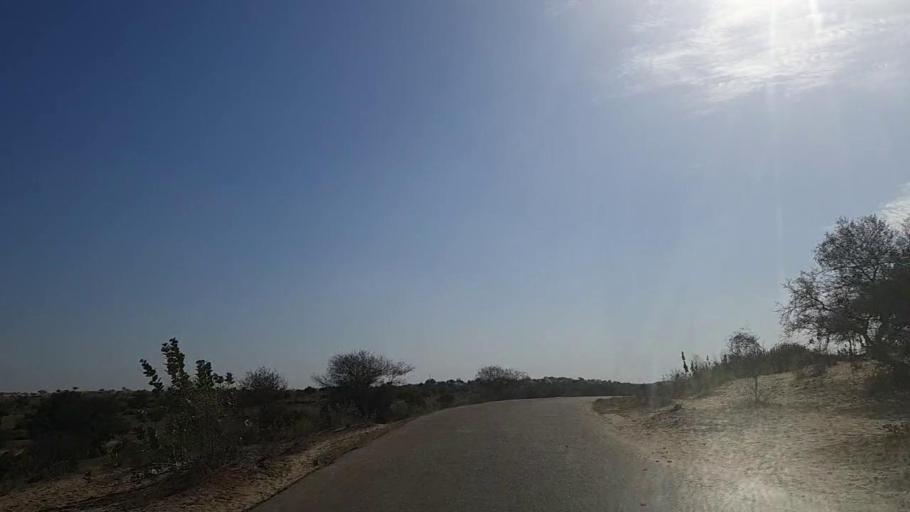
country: PK
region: Sindh
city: Naukot
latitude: 24.8439
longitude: 69.5448
